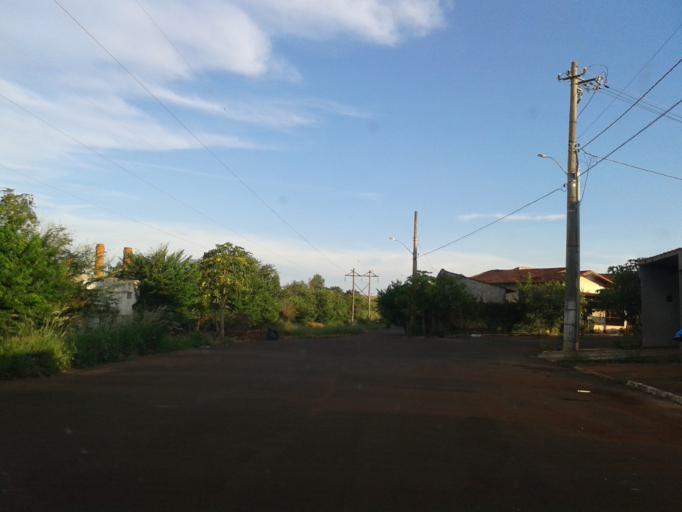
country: BR
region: Minas Gerais
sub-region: Capinopolis
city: Capinopolis
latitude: -18.6911
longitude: -49.5637
